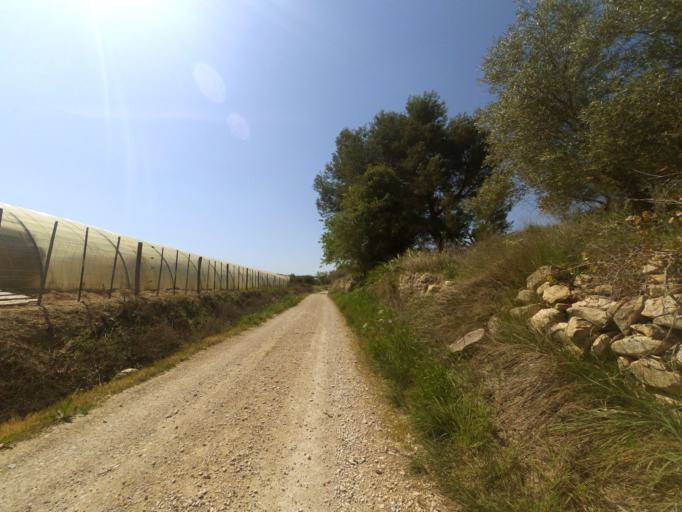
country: FR
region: Languedoc-Roussillon
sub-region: Departement du Gard
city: Congenies
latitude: 43.7786
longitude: 4.1698
